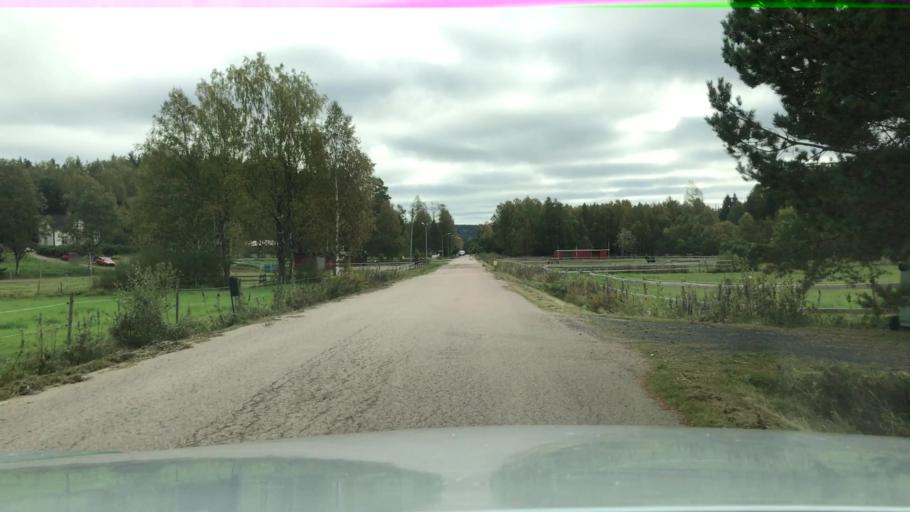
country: SE
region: Vaermland
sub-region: Munkfors Kommun
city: Munkfors
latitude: 59.8389
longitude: 13.5032
